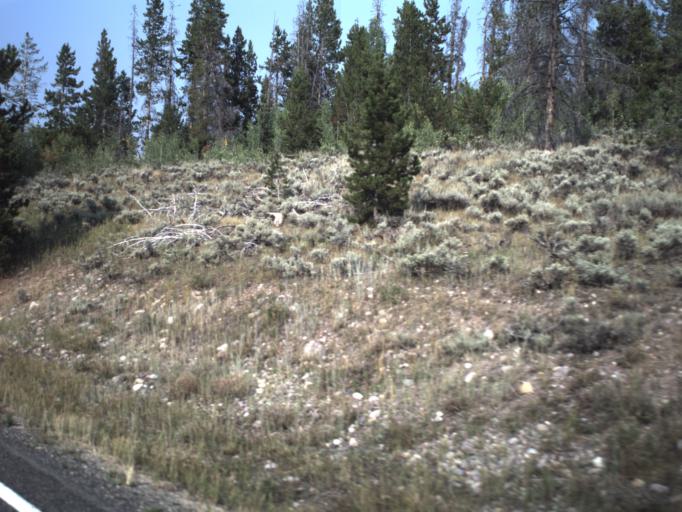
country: US
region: Wyoming
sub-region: Uinta County
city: Evanston
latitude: 40.8880
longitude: -110.8315
